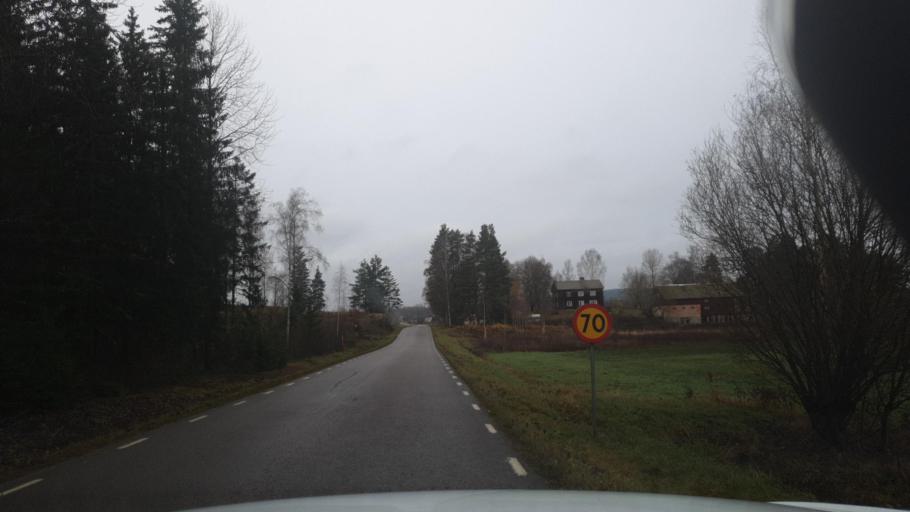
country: SE
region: Vaermland
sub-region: Arvika Kommun
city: Arvika
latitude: 59.5611
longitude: 12.5336
